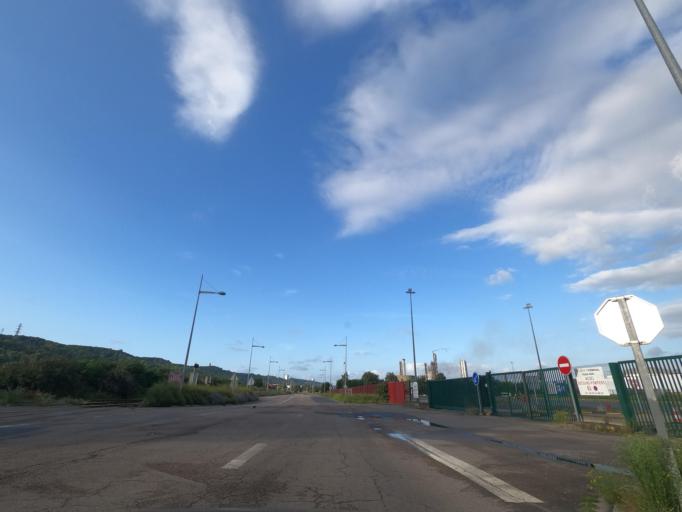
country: FR
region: Haute-Normandie
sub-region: Departement de la Seine-Maritime
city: Petit-Couronne
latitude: 49.4120
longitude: 1.0184
